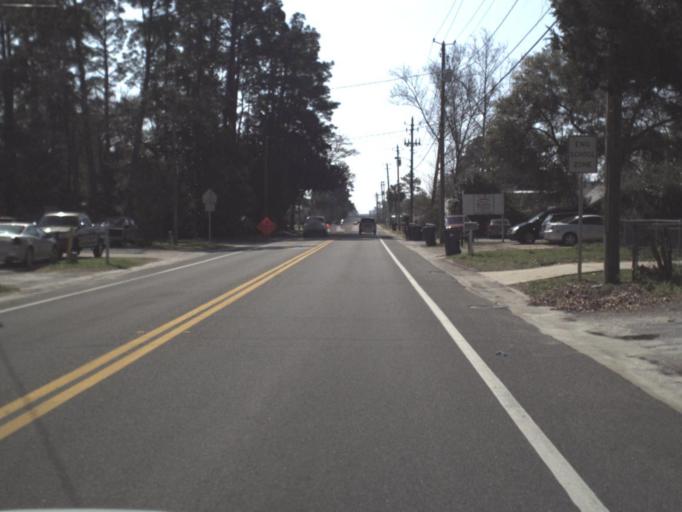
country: US
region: Florida
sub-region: Bay County
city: Pretty Bayou
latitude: 30.1826
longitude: -85.7014
